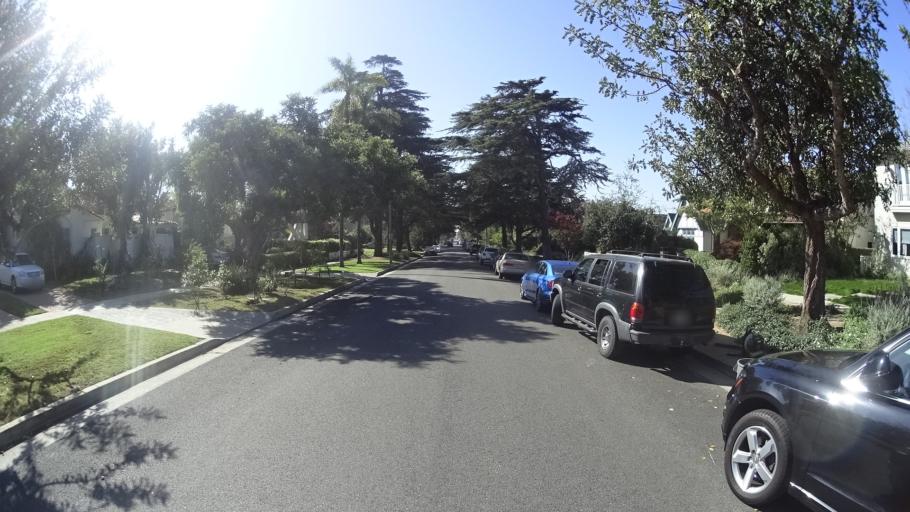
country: US
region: California
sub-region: Los Angeles County
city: Santa Monica
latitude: 34.0377
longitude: -118.4980
